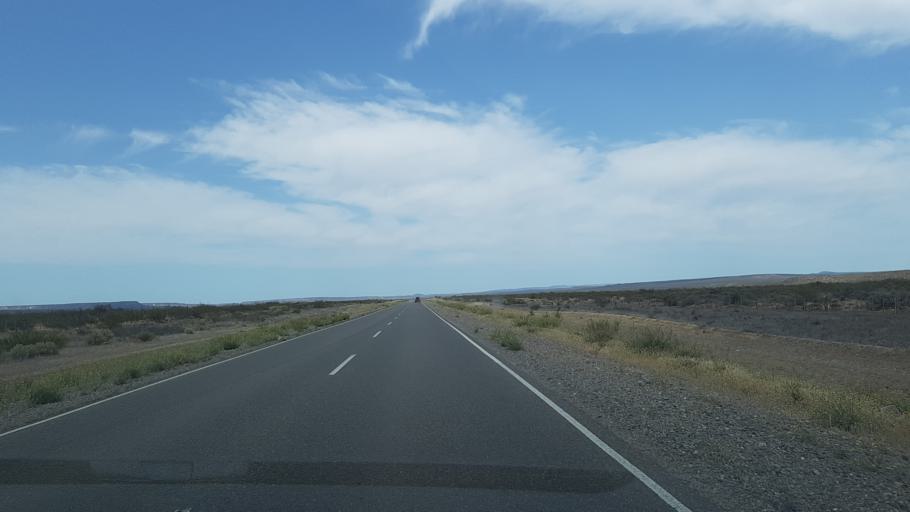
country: AR
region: Neuquen
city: Piedra del Aguila
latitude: -39.8477
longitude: -69.7916
